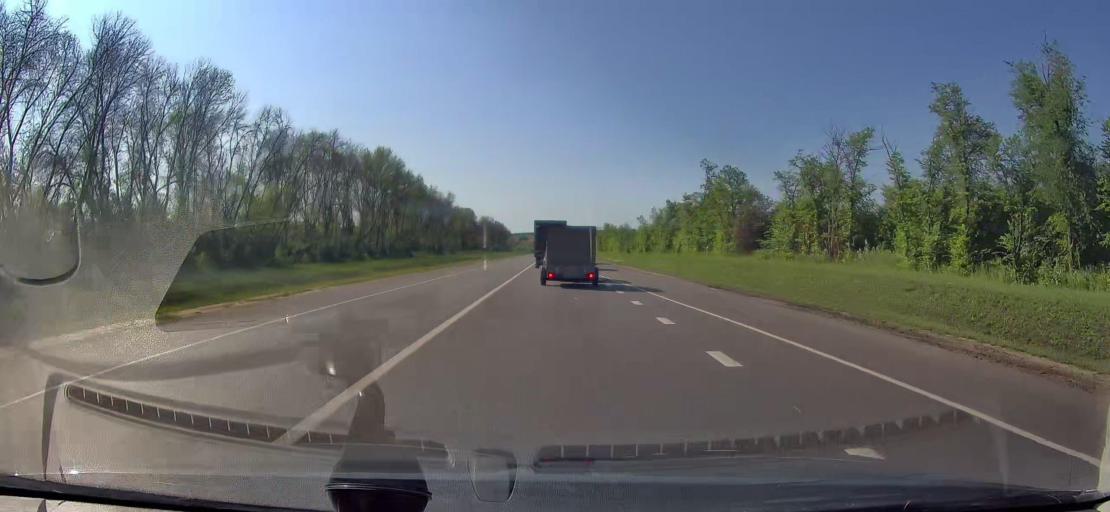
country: RU
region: Orjol
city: Kromy
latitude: 52.6284
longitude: 35.7549
